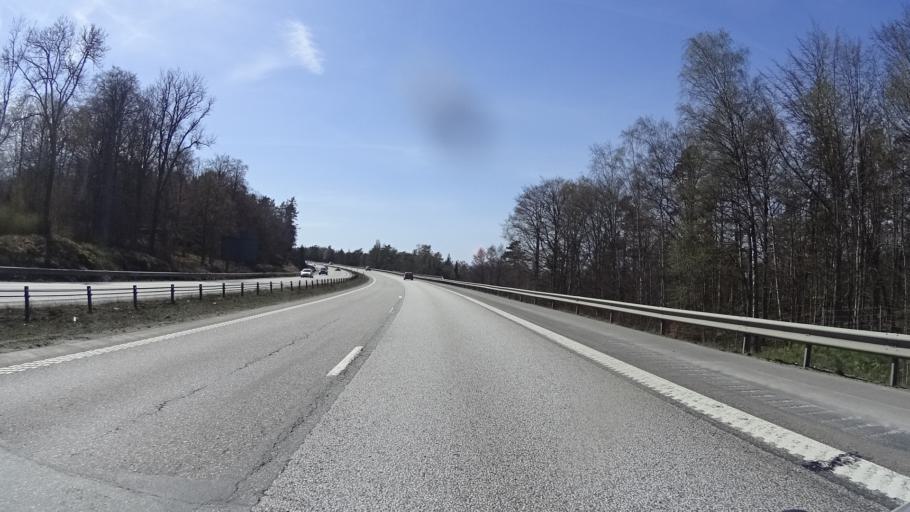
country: SE
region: Joenkoeping
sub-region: Jonkopings Kommun
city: Graenna
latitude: 57.9905
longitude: 14.4188
